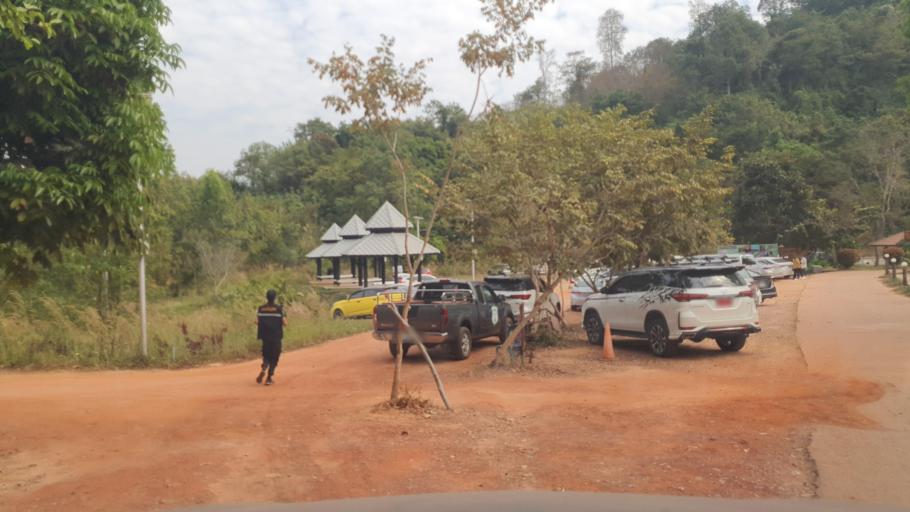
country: TH
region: Changwat Bueng Kan
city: Si Wilai
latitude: 18.2747
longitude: 103.7963
